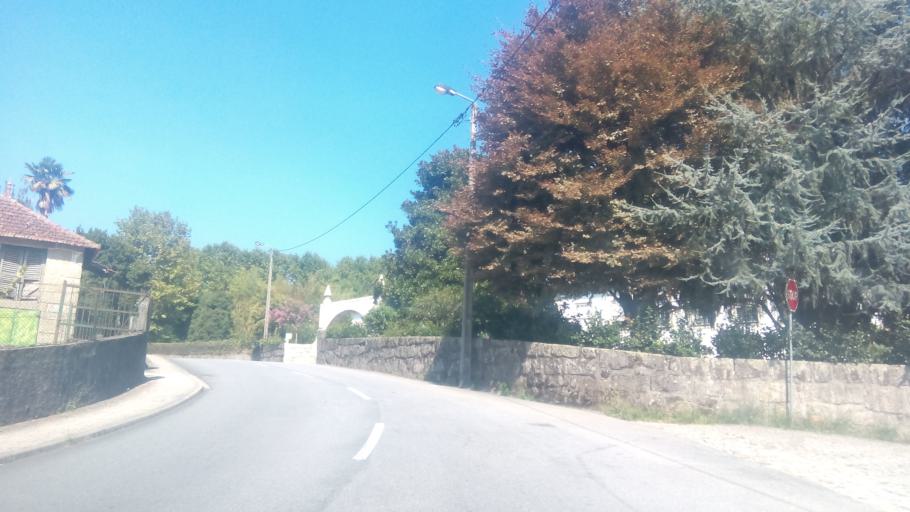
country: PT
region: Porto
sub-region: Paredes
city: Madalena
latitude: 41.2143
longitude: -8.3359
